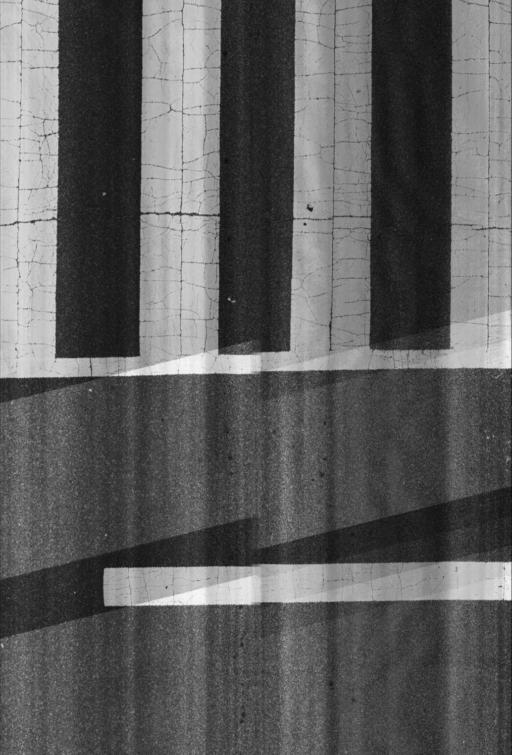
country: US
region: Maryland
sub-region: Montgomery County
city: Friendship Village
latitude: 38.9374
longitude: -77.0686
